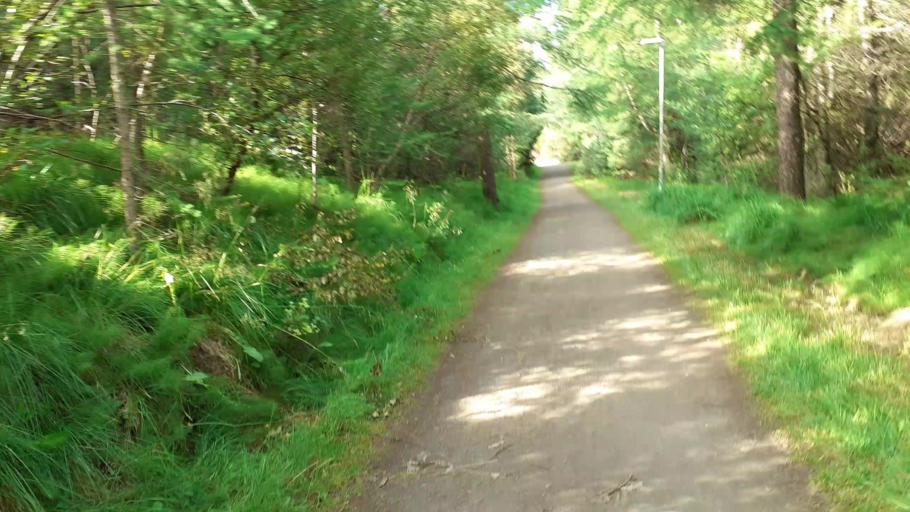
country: IS
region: Northeast
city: Akureyri
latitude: 65.6411
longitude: -18.0954
